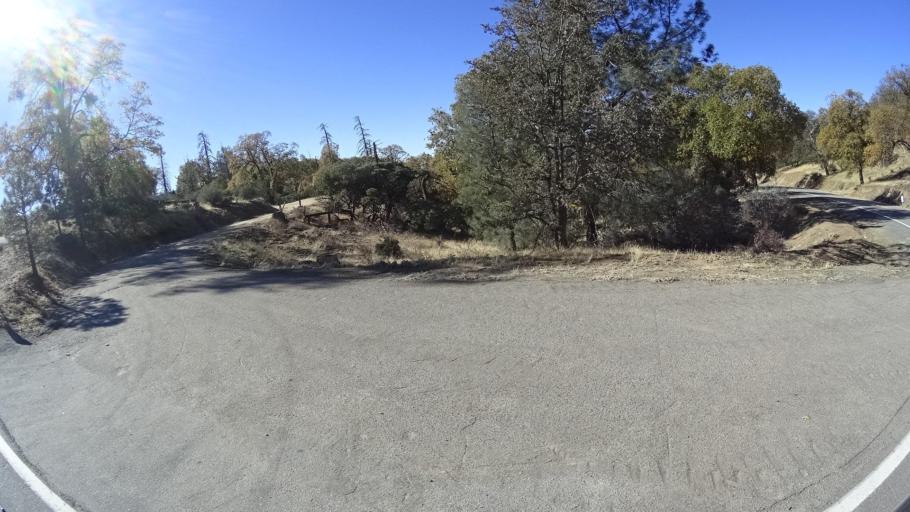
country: US
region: California
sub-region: Kern County
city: Alta Sierra
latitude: 35.7376
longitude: -118.6128
